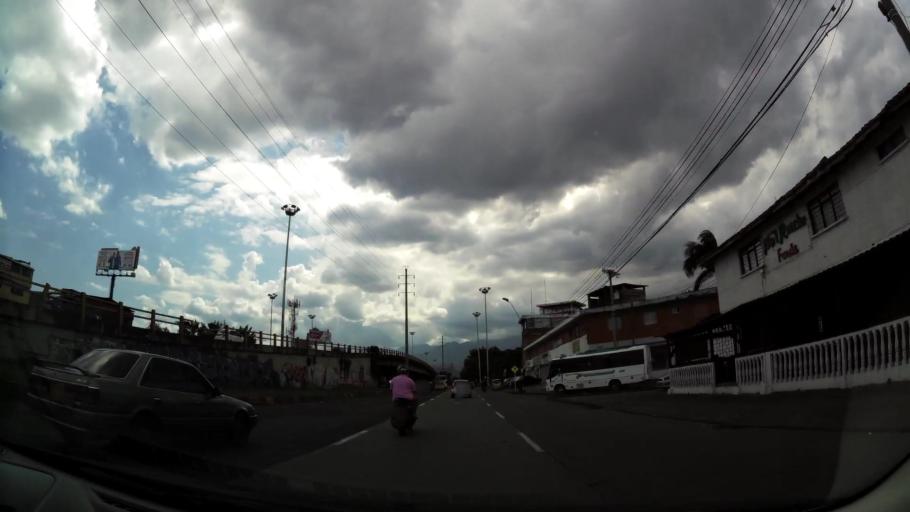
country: CO
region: Valle del Cauca
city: Cali
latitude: 3.4327
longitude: -76.5268
